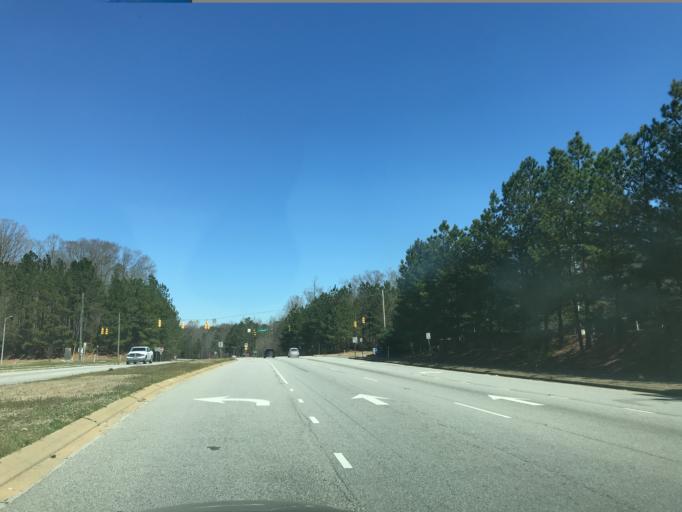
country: US
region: North Carolina
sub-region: Wake County
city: Garner
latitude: 35.7347
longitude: -78.6403
